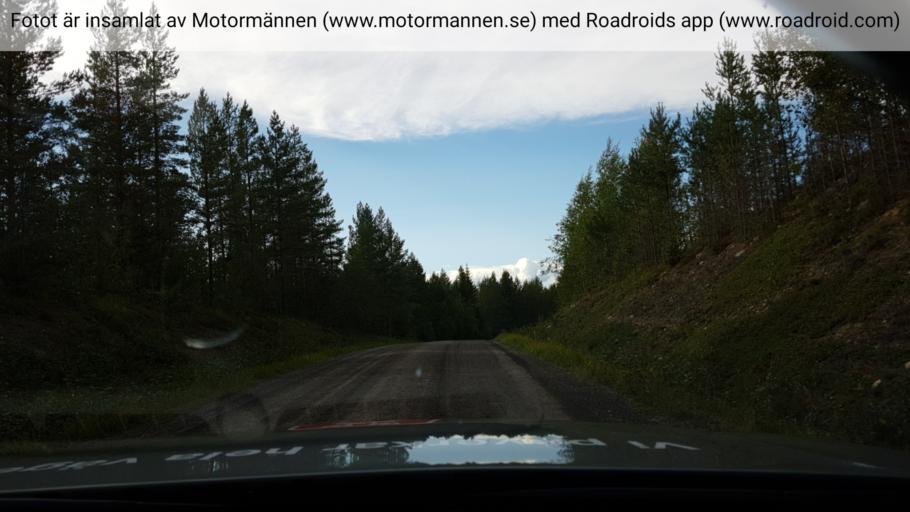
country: SE
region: Jaemtland
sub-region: Braecke Kommun
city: Braecke
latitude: 63.2171
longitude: 15.3532
